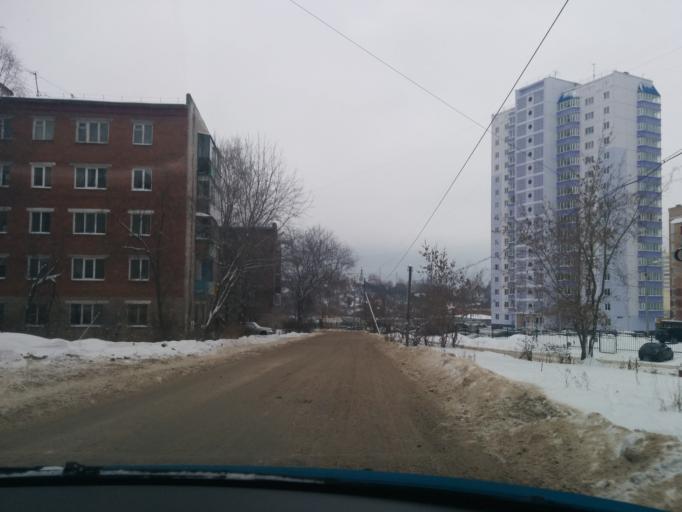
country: RU
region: Perm
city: Perm
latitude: 58.0152
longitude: 56.3008
